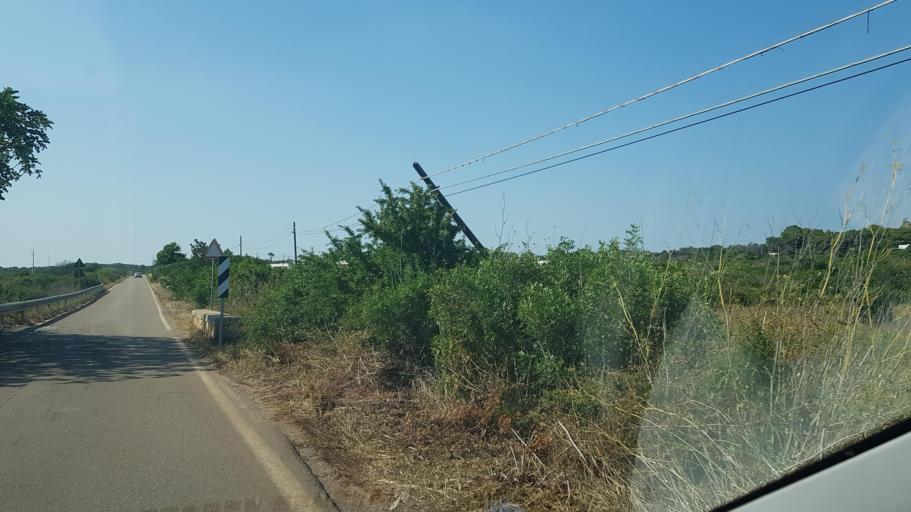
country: IT
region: Apulia
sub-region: Provincia di Lecce
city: Gemini
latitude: 39.8512
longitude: 18.2087
